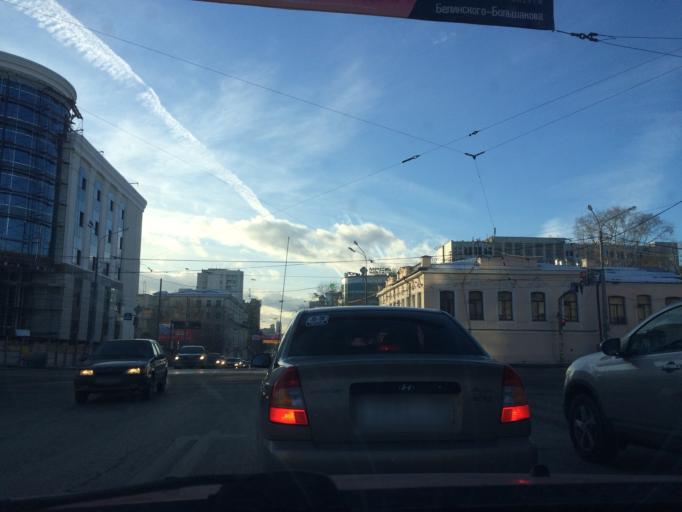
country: RU
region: Sverdlovsk
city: Yekaterinburg
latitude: 56.8296
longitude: 60.6249
